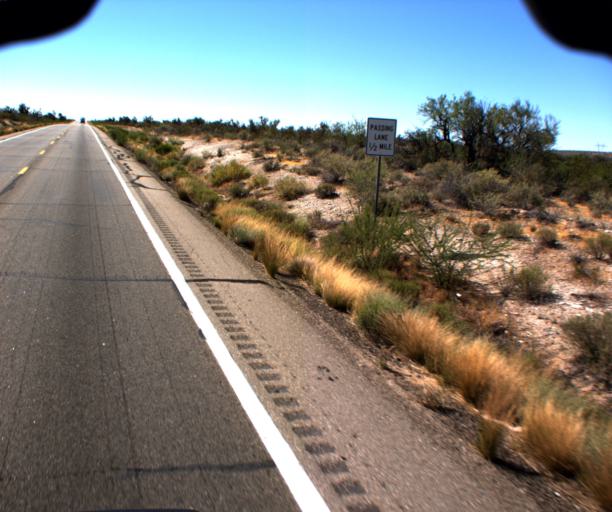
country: US
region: Arizona
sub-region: Yavapai County
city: Bagdad
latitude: 34.2957
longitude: -113.1147
